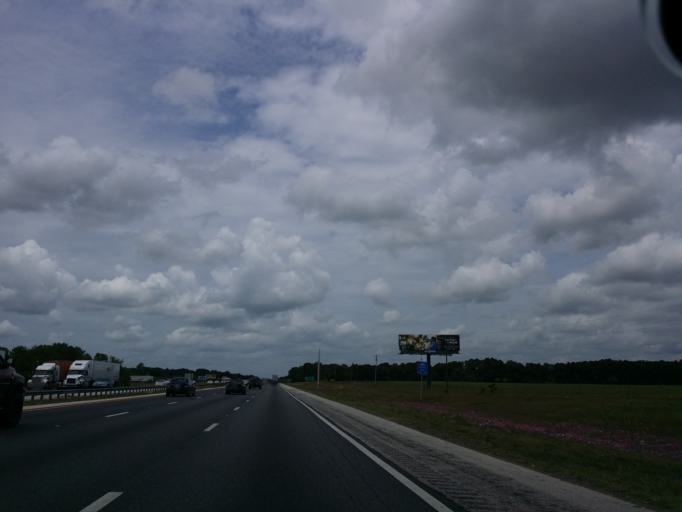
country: US
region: Florida
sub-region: Sumter County
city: Wildwood
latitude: 28.8857
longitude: -82.0951
